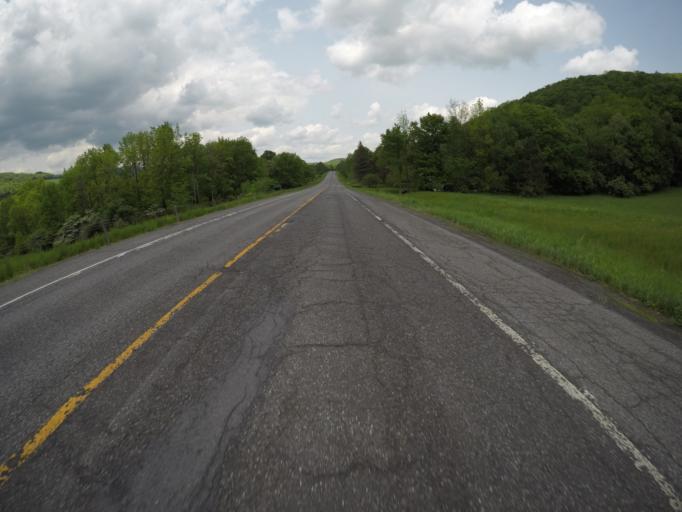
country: US
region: New York
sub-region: Delaware County
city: Stamford
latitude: 42.2544
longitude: -74.5943
